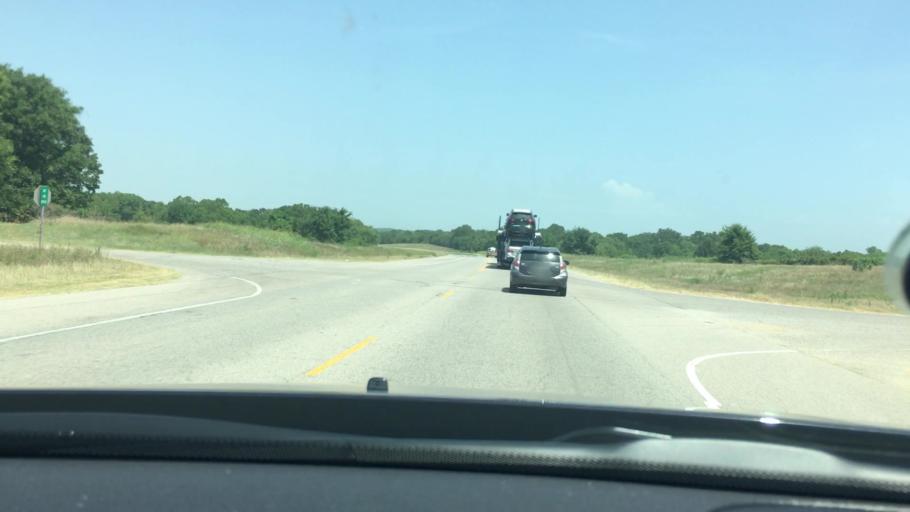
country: US
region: Oklahoma
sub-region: Pontotoc County
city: Ada
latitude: 34.6942
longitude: -96.5972
